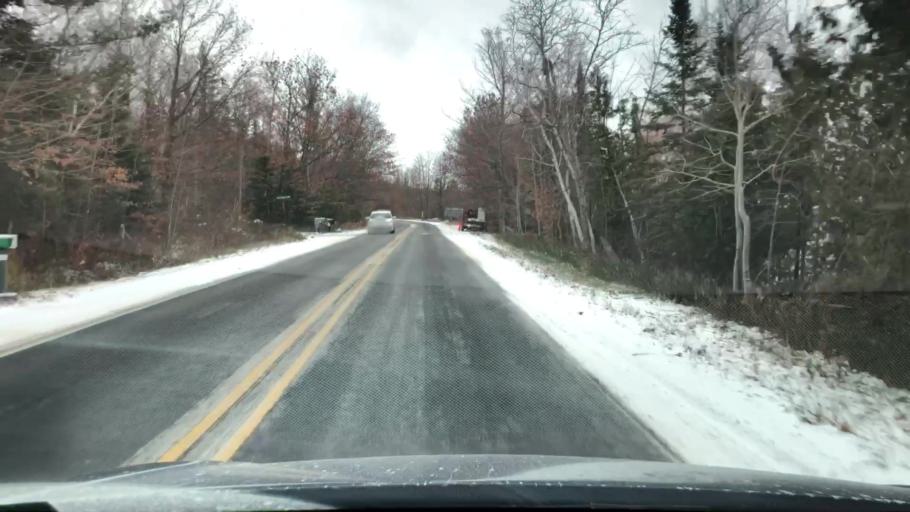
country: US
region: Michigan
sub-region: Leelanau County
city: Greilickville
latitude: 44.8347
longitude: -85.5626
